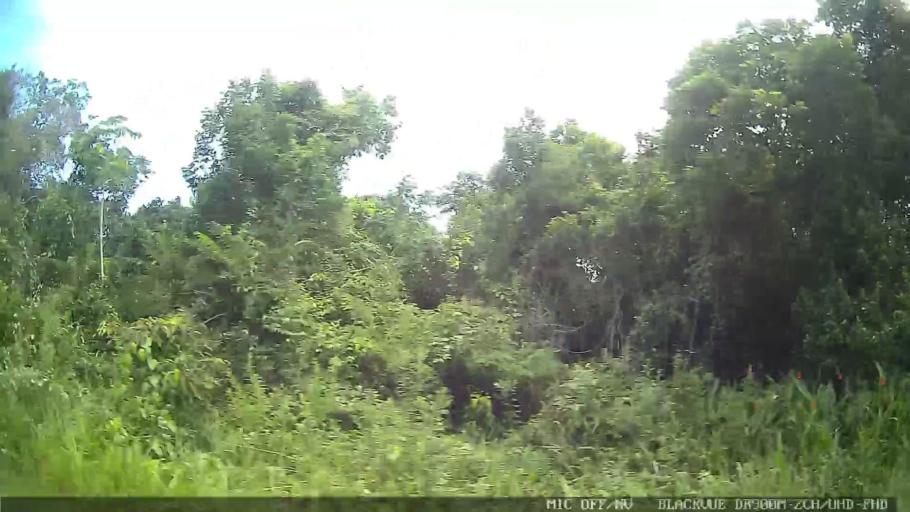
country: BR
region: Sao Paulo
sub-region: Iguape
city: Iguape
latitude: -24.6622
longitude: -47.4194
